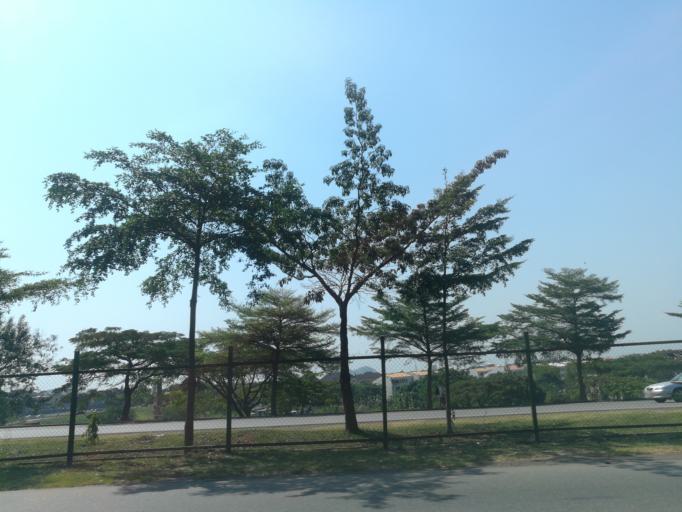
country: NG
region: Abuja Federal Capital Territory
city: Abuja
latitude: 9.0789
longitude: 7.4535
